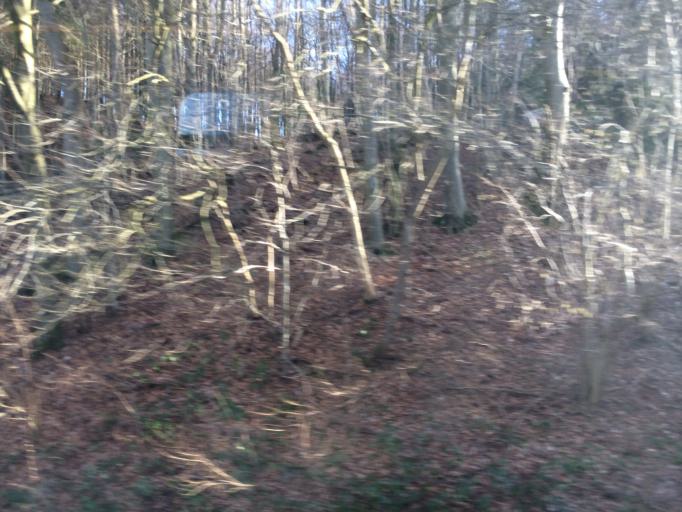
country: DK
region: South Denmark
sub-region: Vejle Kommune
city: Vejle
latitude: 55.7506
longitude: 9.5350
